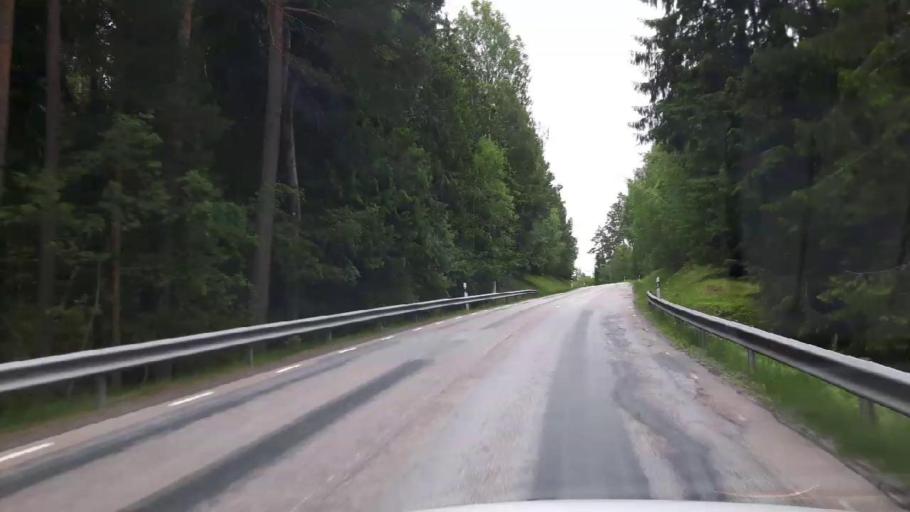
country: SE
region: Vaestmanland
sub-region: Kopings Kommun
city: Kolsva
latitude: 59.6323
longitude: 15.8025
